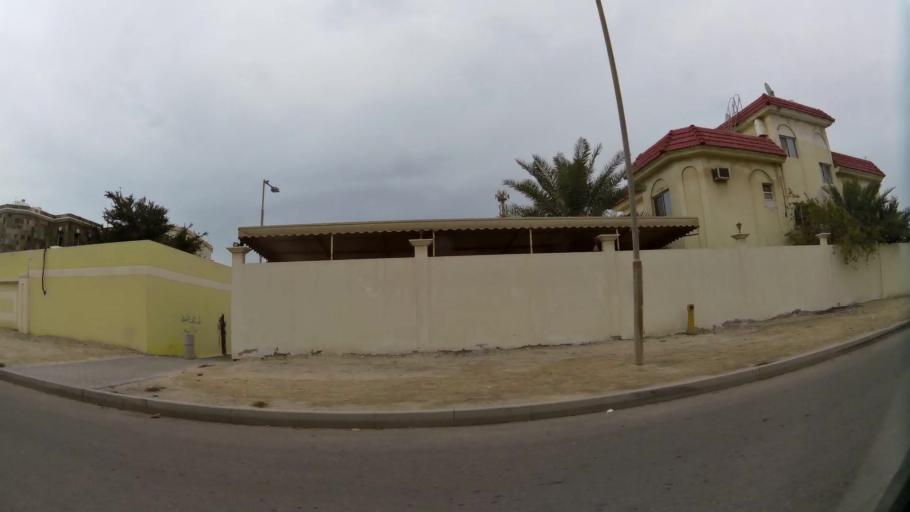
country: BH
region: Central Governorate
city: Madinat Hamad
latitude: 26.1073
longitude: 50.5017
